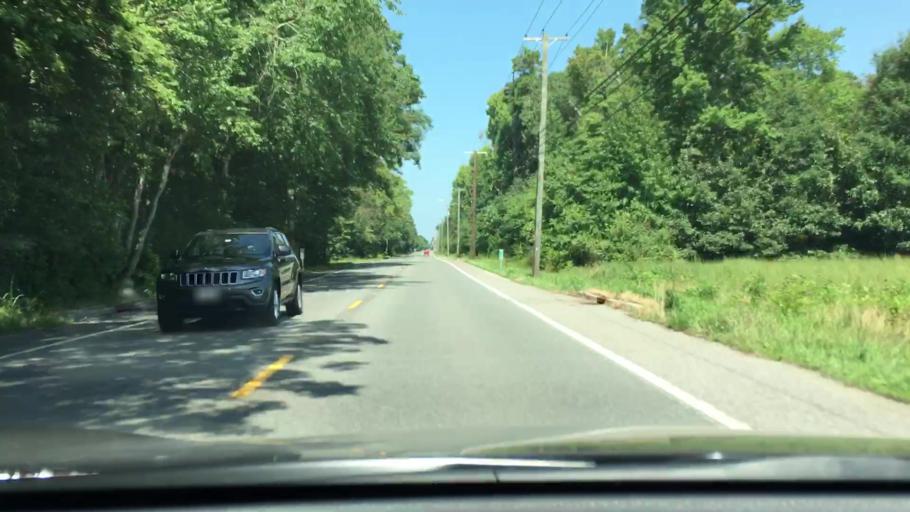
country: US
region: New Jersey
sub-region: Cumberland County
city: Laurel Lake
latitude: 39.3095
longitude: -75.0070
